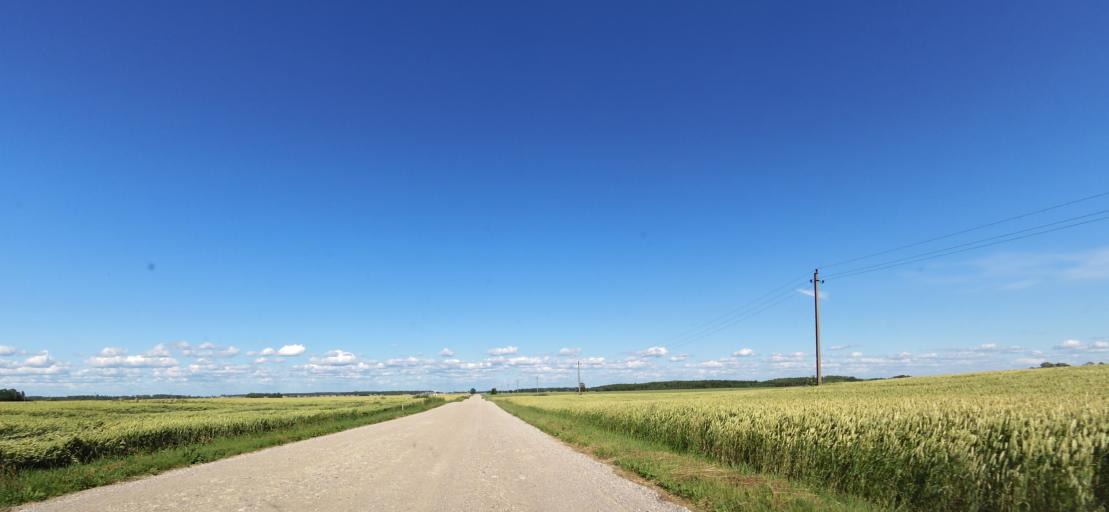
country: LT
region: Panevezys
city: Pasvalys
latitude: 56.1221
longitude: 24.3543
